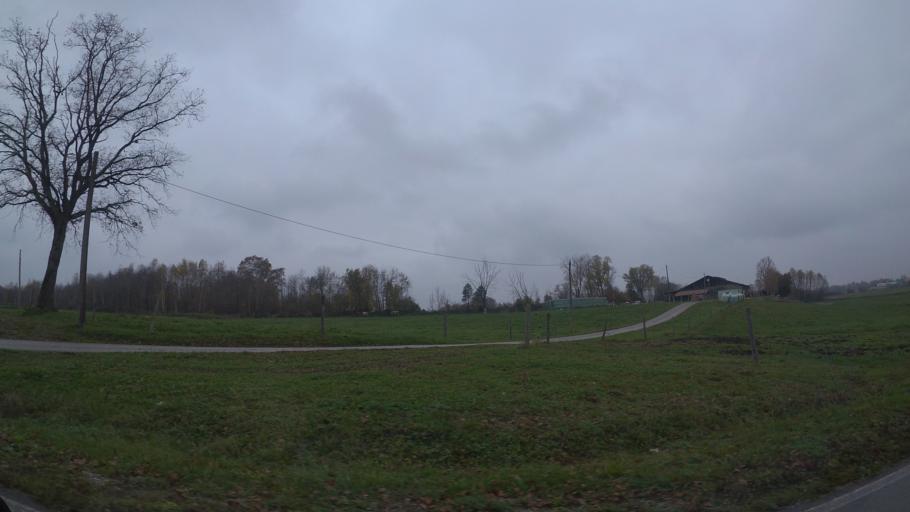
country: HR
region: Karlovacka
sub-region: Grad Karlovac
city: Karlovac
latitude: 45.4842
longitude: 15.5900
